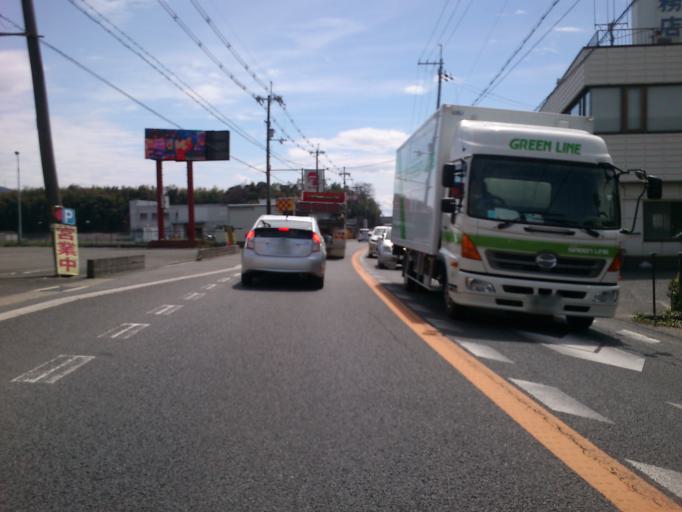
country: JP
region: Kyoto
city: Tanabe
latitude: 34.8356
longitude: 135.7919
